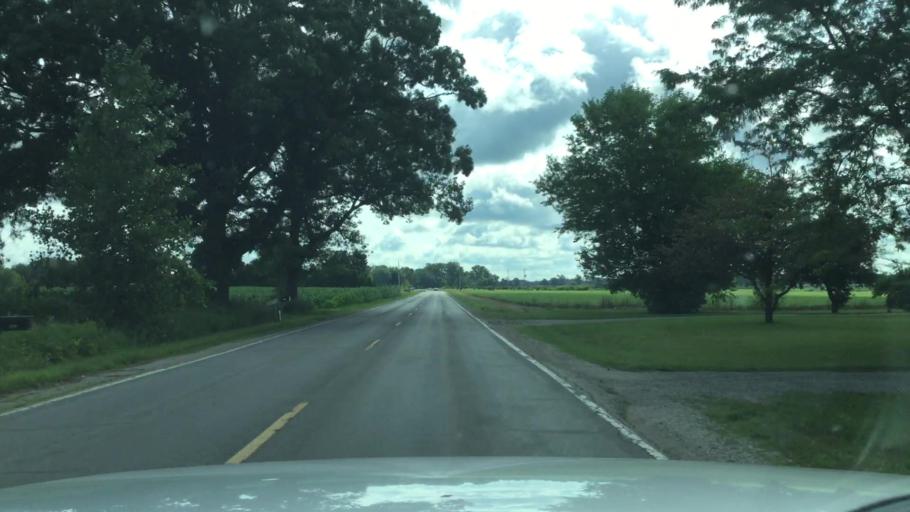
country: US
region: Michigan
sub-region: Montcalm County
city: Greenville
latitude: 43.1922
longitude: -85.1989
